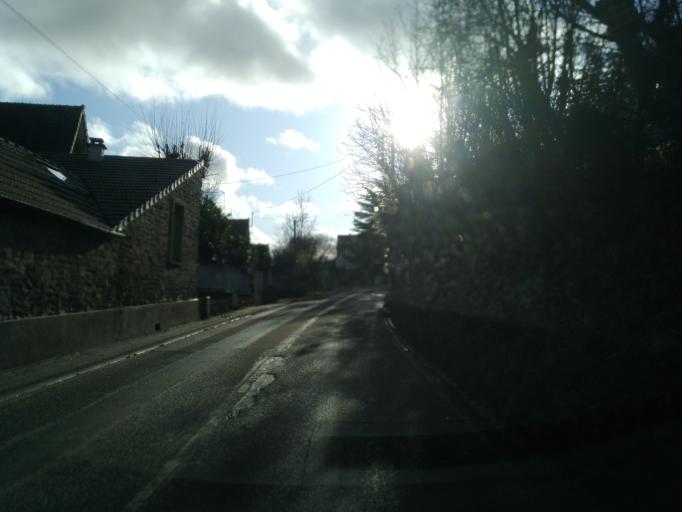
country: FR
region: Ile-de-France
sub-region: Departement des Yvelines
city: Beynes
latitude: 48.8593
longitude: 1.8729
